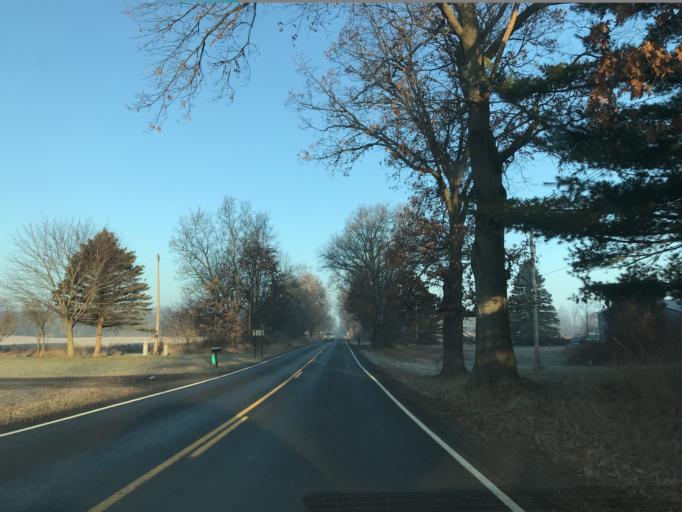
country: US
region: Michigan
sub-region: Ingham County
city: Leslie
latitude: 42.3790
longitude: -84.4483
